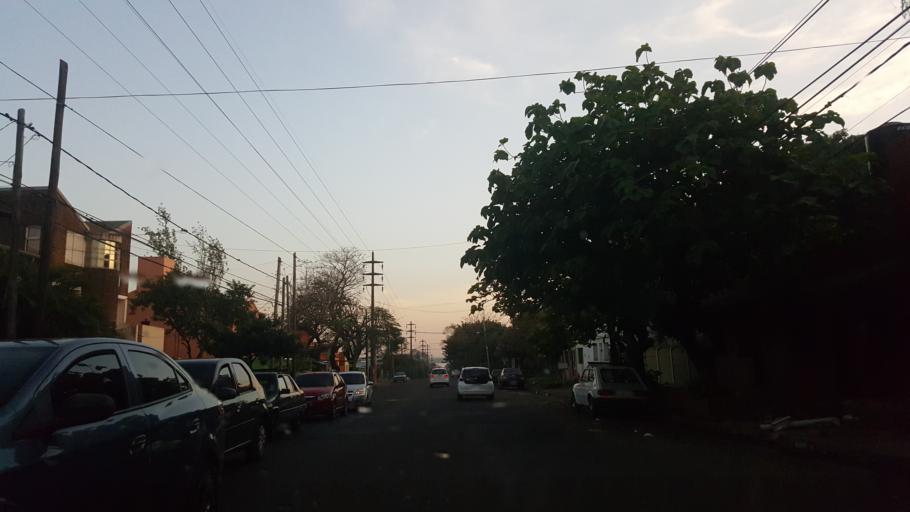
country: AR
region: Misiones
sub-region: Departamento de Capital
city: Posadas
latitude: -27.3664
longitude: -55.9050
